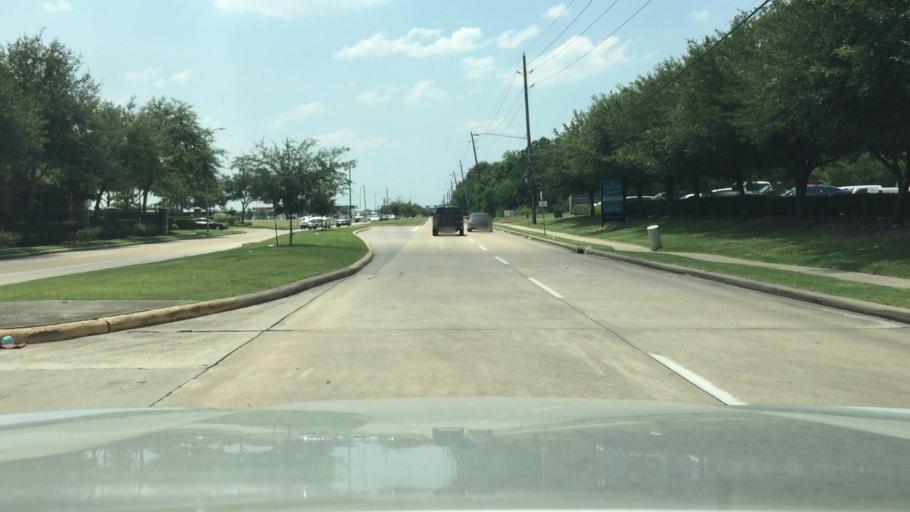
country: US
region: Texas
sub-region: Harris County
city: Bunker Hill Village
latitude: 29.7281
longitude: -95.5925
